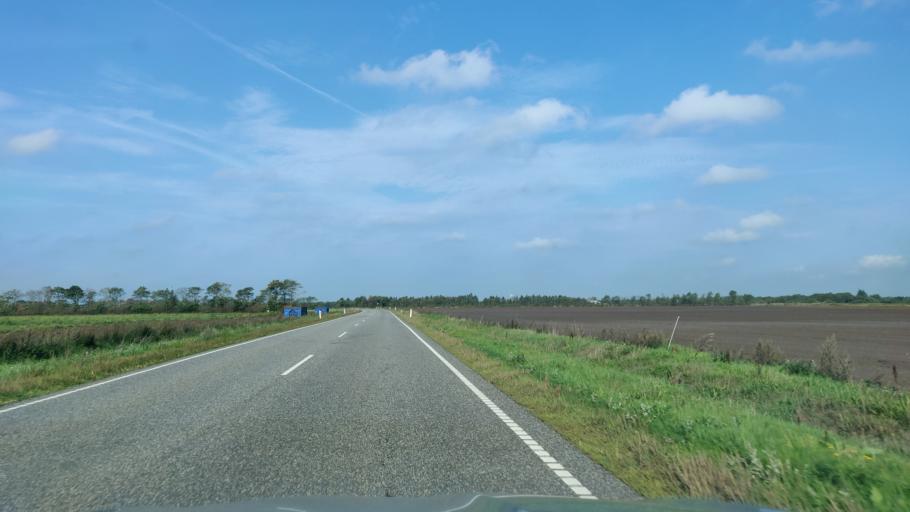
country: DK
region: Central Jutland
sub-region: Herning Kommune
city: Sunds
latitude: 56.2635
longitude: 9.0222
